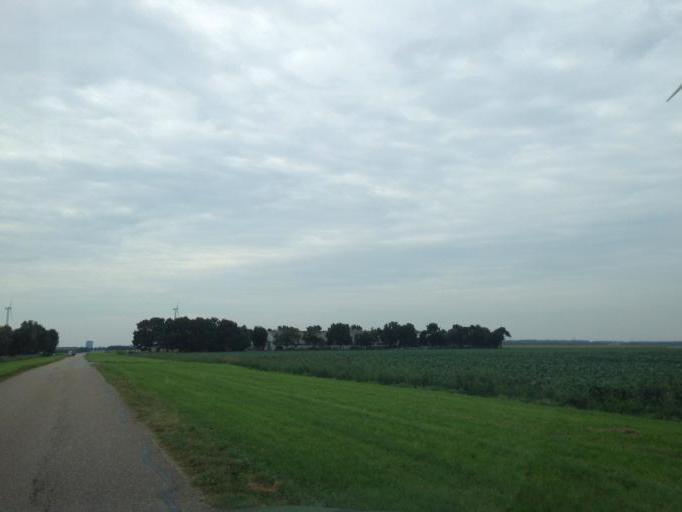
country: NL
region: Utrecht
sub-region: Gemeente Bunschoten
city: Spakenburg
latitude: 52.3715
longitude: 5.3437
